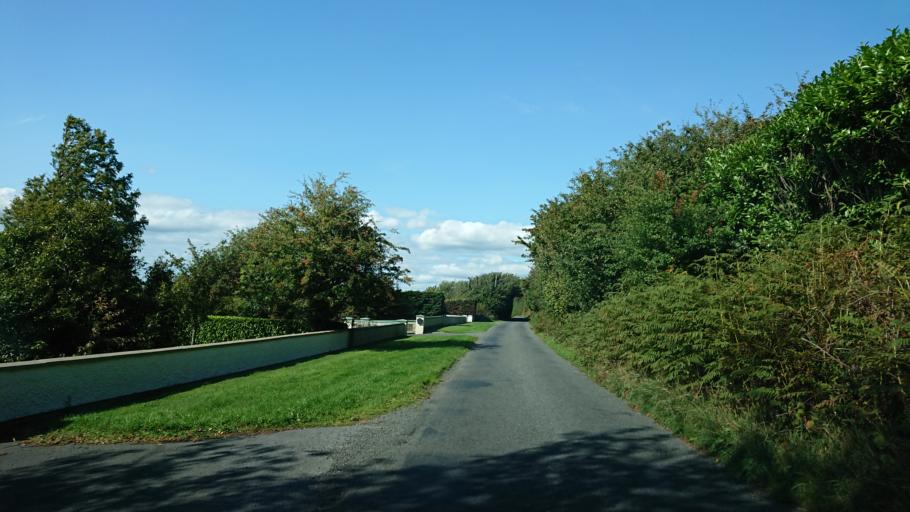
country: IE
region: Munster
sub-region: Waterford
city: Waterford
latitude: 52.2224
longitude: -7.0567
